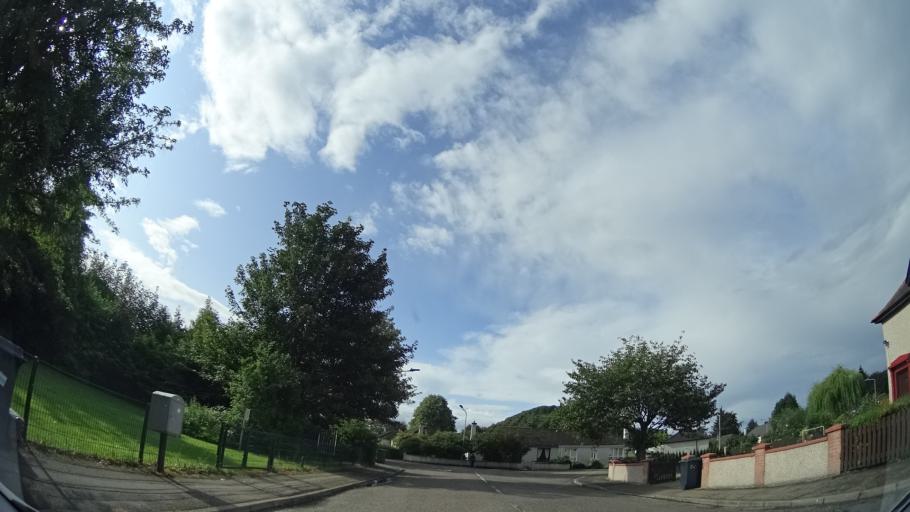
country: GB
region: Scotland
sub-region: Highland
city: Inverness
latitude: 57.4733
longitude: -4.2398
